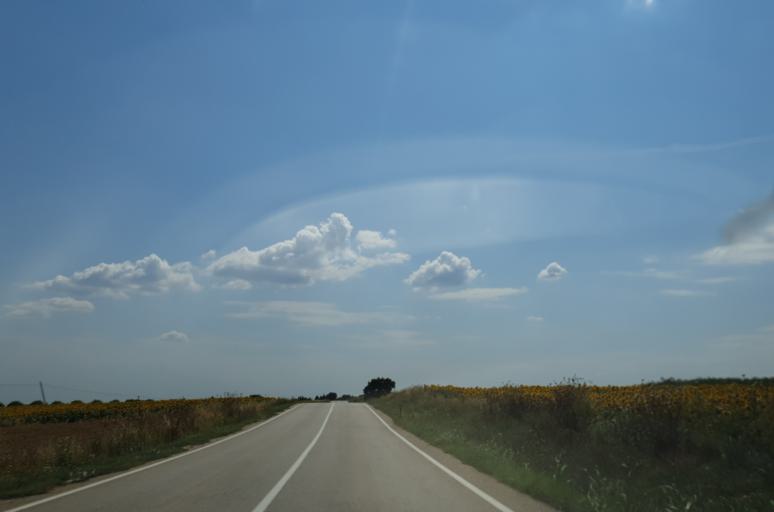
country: TR
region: Kirklareli
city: Vize
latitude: 41.4820
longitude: 27.6847
